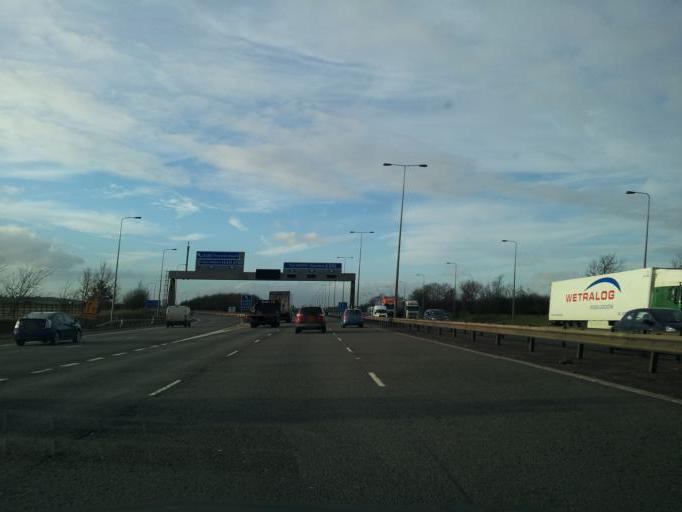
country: GB
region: England
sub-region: Cambridgeshire
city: Stilton
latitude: 52.5264
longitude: -0.3113
